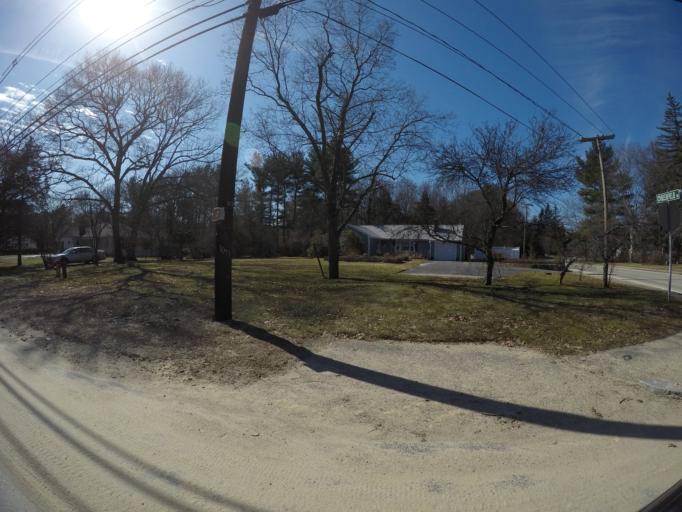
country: US
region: Massachusetts
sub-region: Norfolk County
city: Stoughton
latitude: 42.1131
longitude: -71.1356
